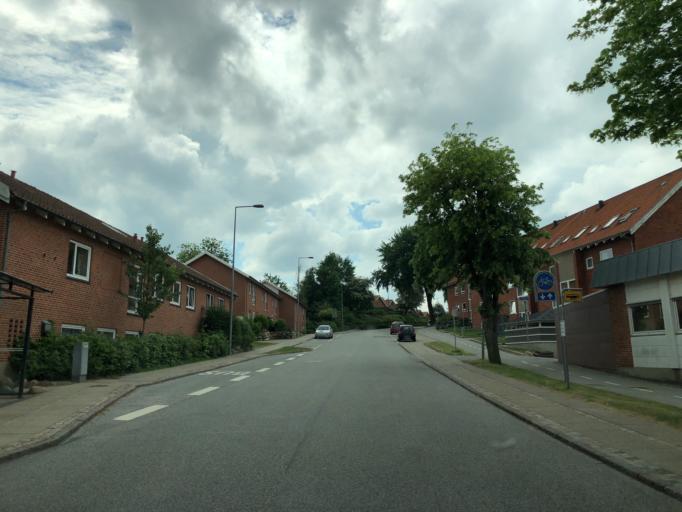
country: DK
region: Central Jutland
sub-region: Struer Kommune
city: Struer
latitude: 56.4904
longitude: 8.5909
